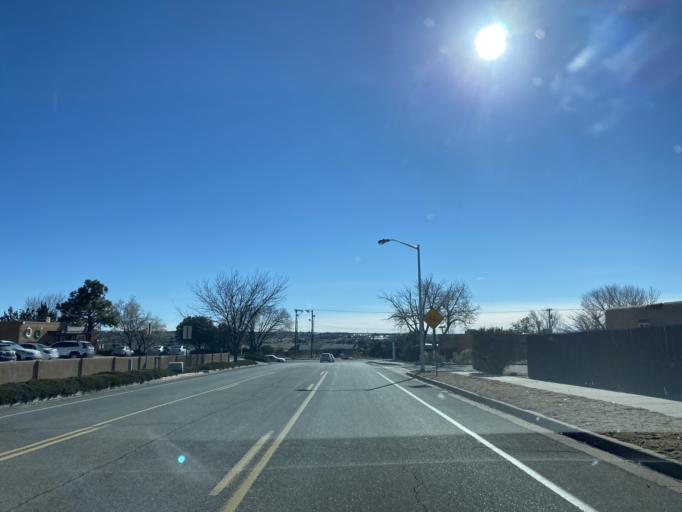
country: US
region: New Mexico
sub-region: Santa Fe County
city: Santa Fe
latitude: 35.6530
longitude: -105.9585
